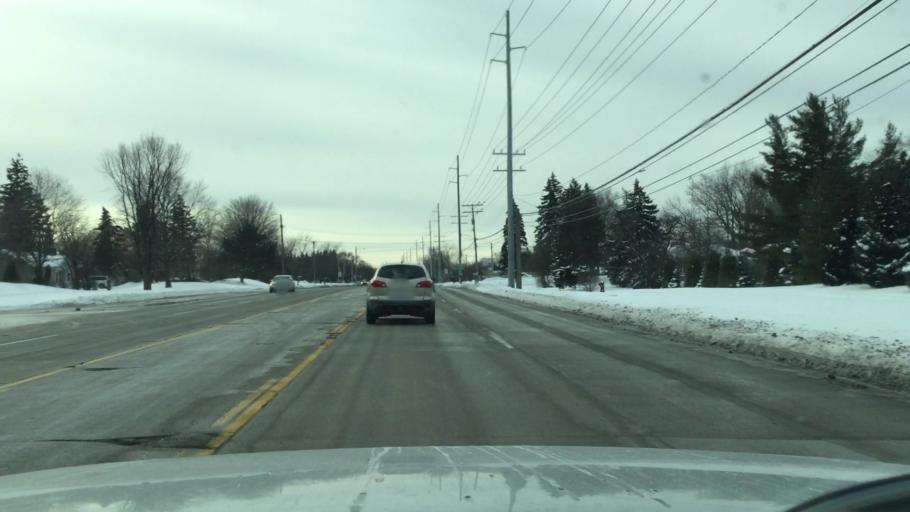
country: US
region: Michigan
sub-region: Oakland County
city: Troy
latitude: 42.6101
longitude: -83.1300
